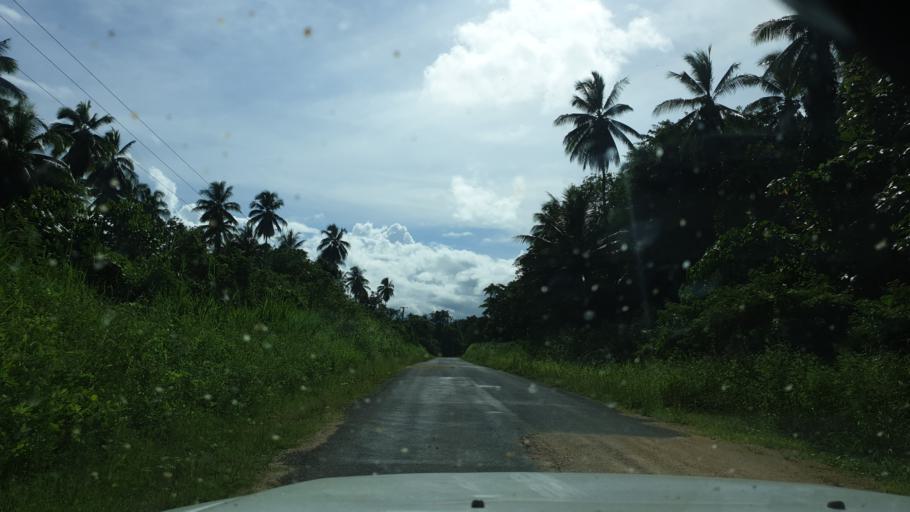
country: PG
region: Madang
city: Madang
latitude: -4.9308
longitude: 145.7778
